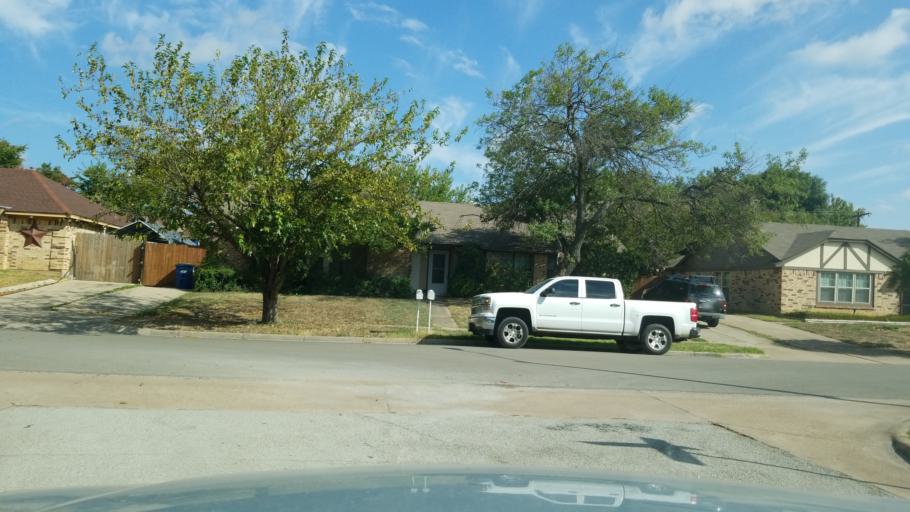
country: US
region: Texas
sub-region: Tarrant County
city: Euless
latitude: 32.8488
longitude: -97.0811
